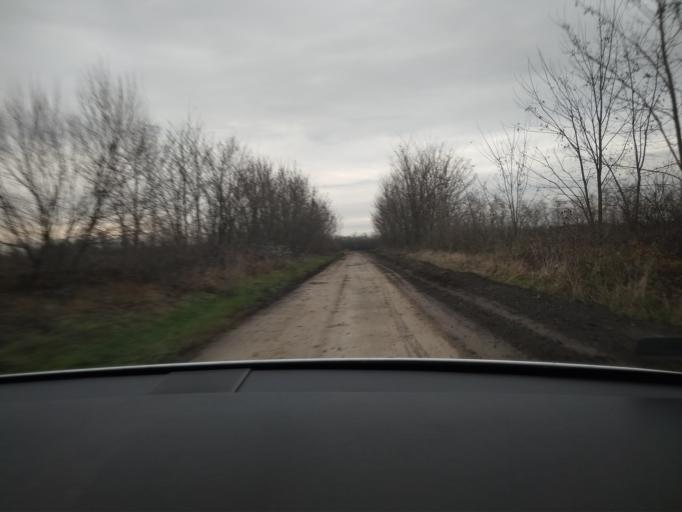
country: HU
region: Szabolcs-Szatmar-Bereg
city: Apagy
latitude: 47.9934
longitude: 21.8972
